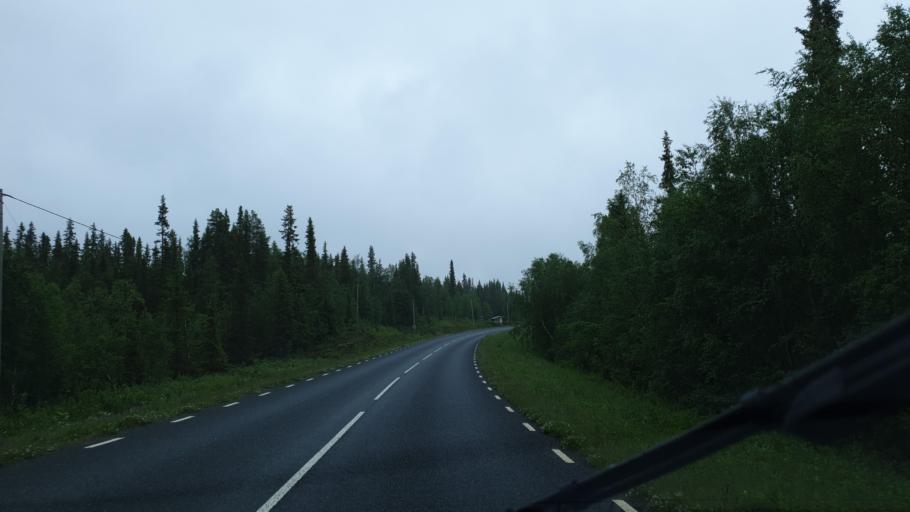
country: SE
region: Vaesterbotten
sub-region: Vilhelmina Kommun
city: Sjoberg
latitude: 65.2479
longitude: 15.7413
